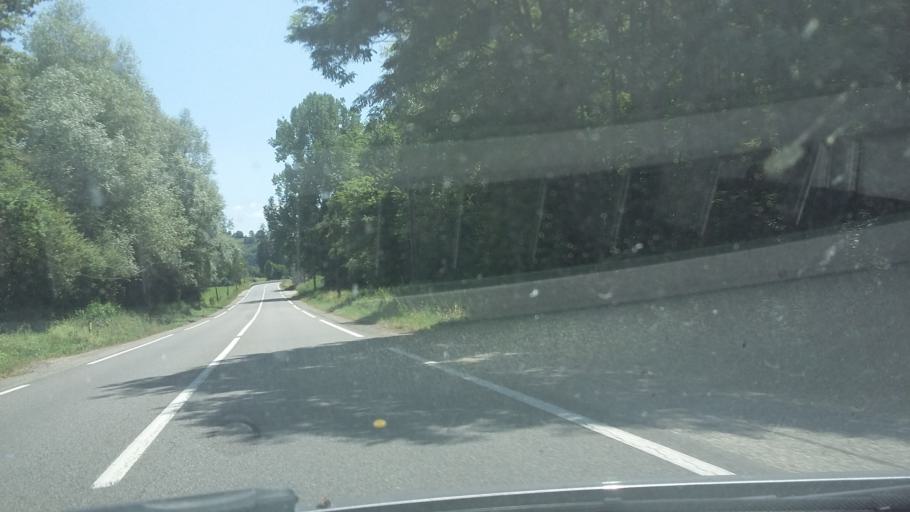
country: FR
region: Rhone-Alpes
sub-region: Departement de l'Ain
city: Belley
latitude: 45.7827
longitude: 5.6878
